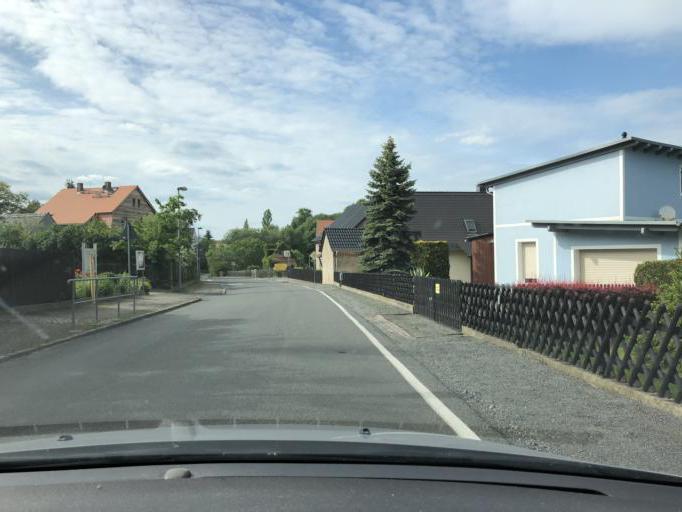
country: DE
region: Saxony
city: Trebsen
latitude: 51.2902
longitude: 12.6966
